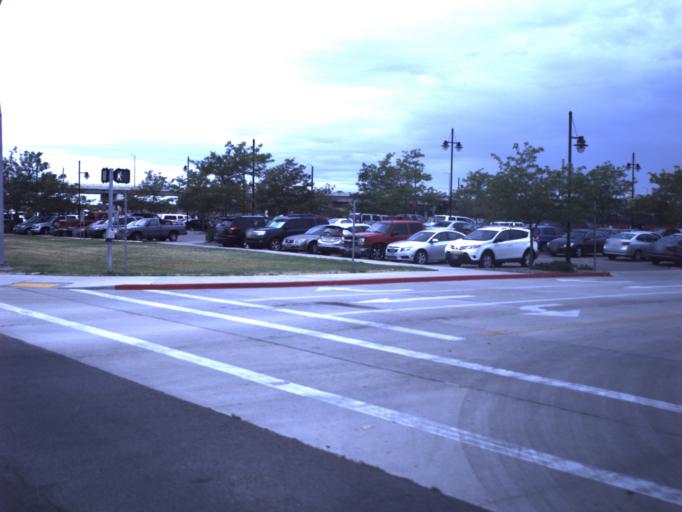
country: US
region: Utah
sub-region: Weber County
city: Ogden
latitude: 41.2251
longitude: -111.9789
